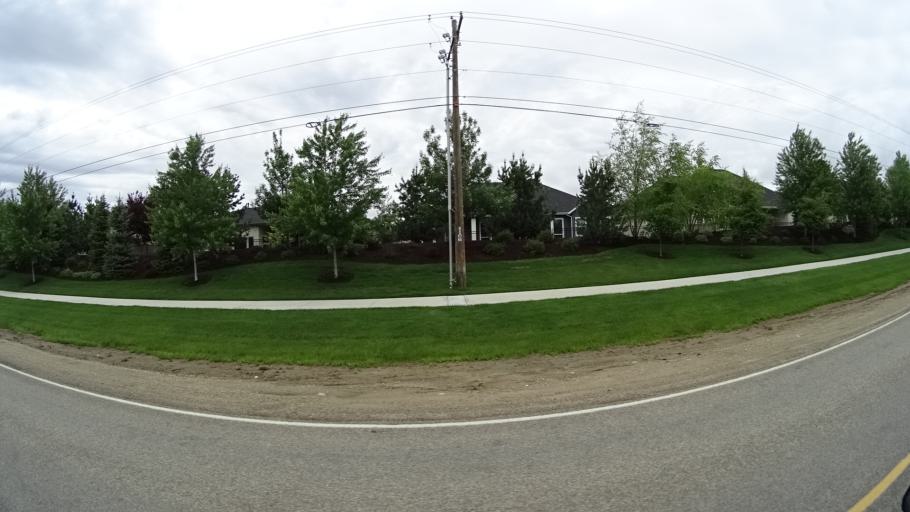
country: US
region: Idaho
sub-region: Ada County
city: Star
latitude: 43.7078
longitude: -116.4324
